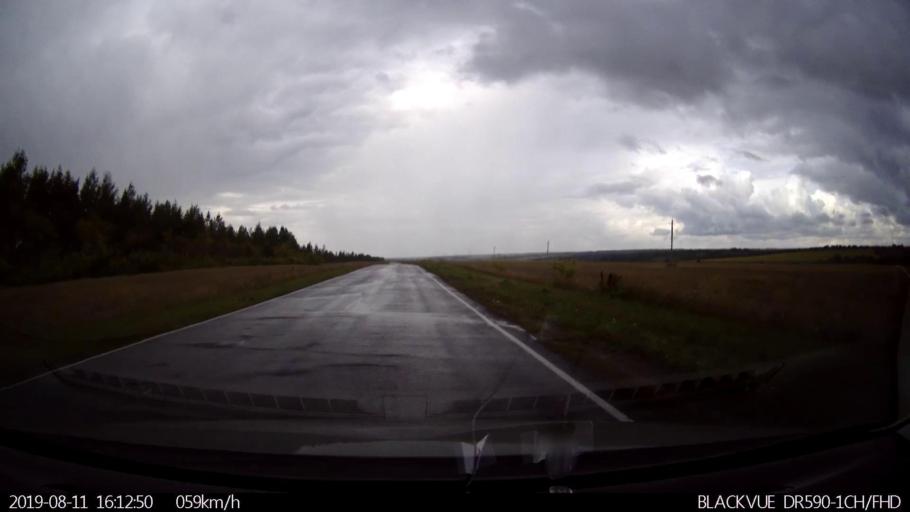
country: RU
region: Ulyanovsk
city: Ignatovka
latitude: 54.0149
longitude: 47.6391
